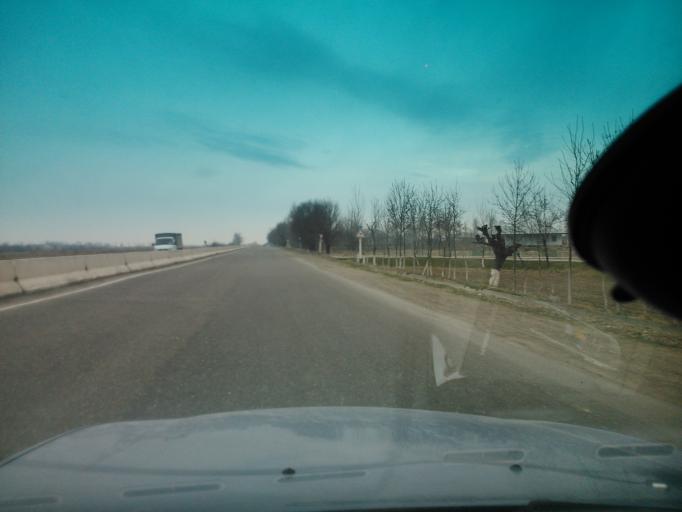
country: UZ
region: Sirdaryo
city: Guliston
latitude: 40.4212
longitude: 68.7843
